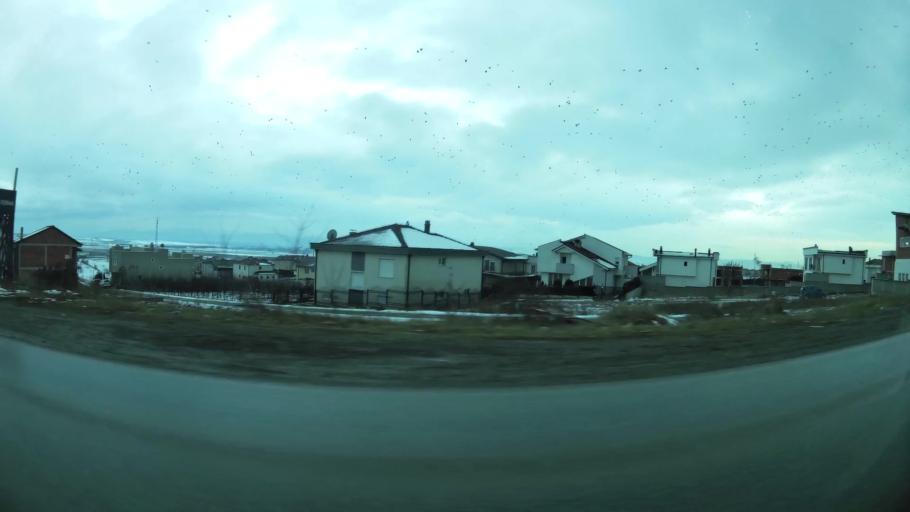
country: XK
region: Pristina
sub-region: Komuna e Prishtines
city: Pristina
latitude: 42.6223
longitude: 21.1619
